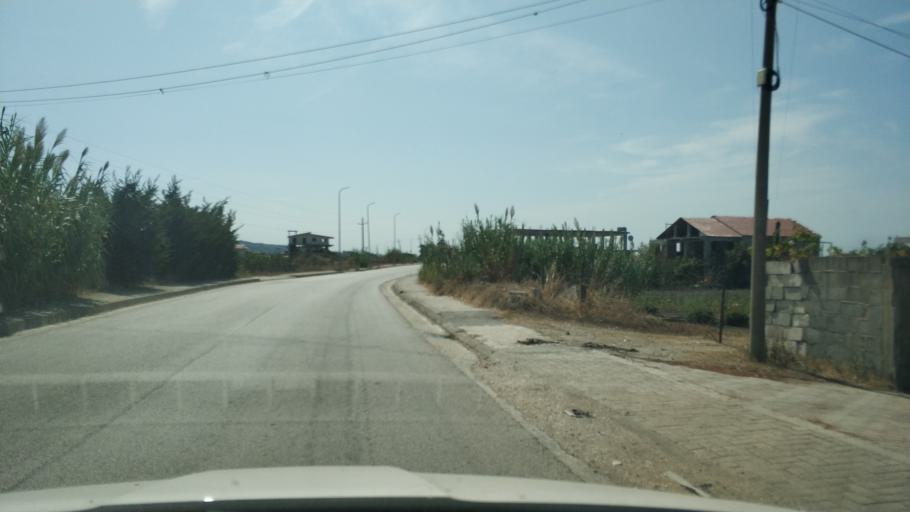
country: AL
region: Fier
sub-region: Rrethi i Lushnjes
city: Divjake
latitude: 40.9865
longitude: 19.5346
